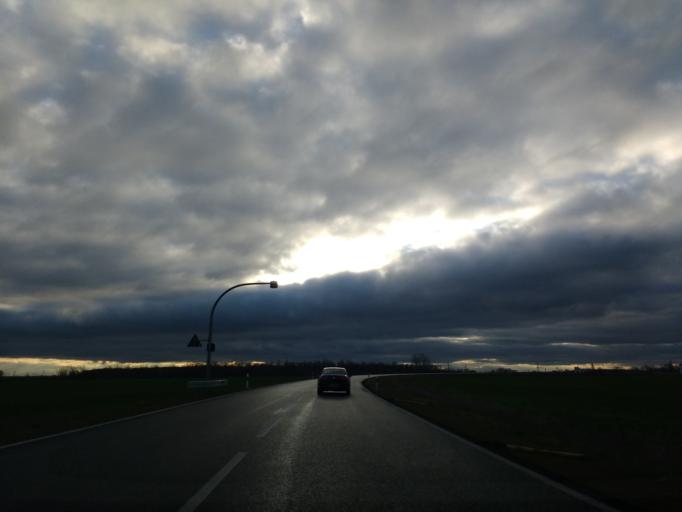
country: DE
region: Saxony-Anhalt
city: Zscherben
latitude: 51.3210
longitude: 11.9732
